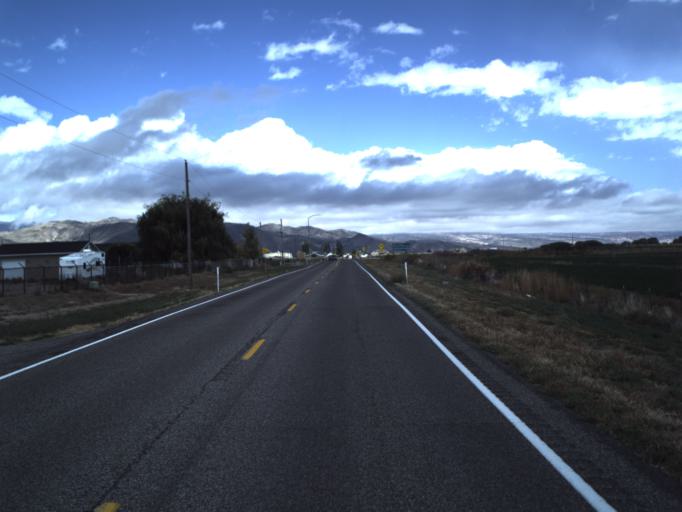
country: US
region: Utah
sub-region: Sevier County
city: Monroe
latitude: 38.6811
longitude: -112.1216
